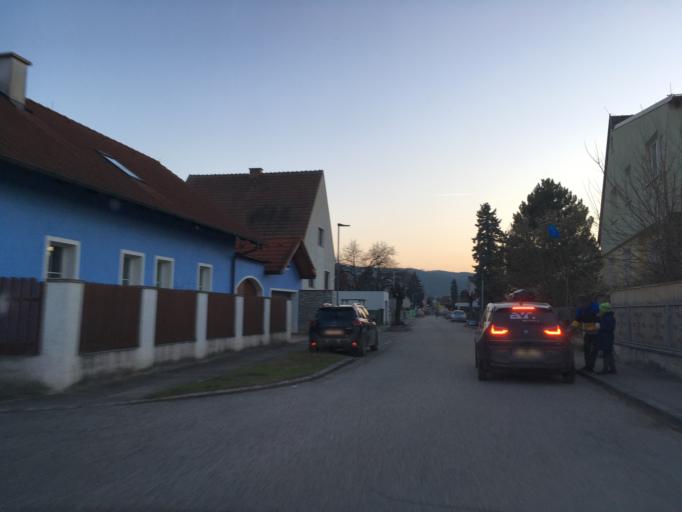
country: AT
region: Lower Austria
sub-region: Politischer Bezirk Tulln
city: Wordern
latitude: 48.3341
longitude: 16.2146
